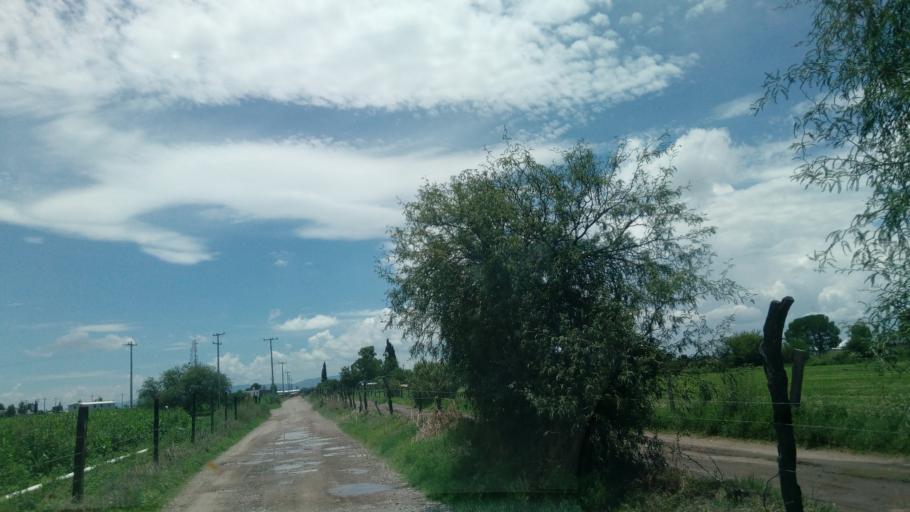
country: MX
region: Durango
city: Victoria de Durango
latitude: 24.0856
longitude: -104.5569
